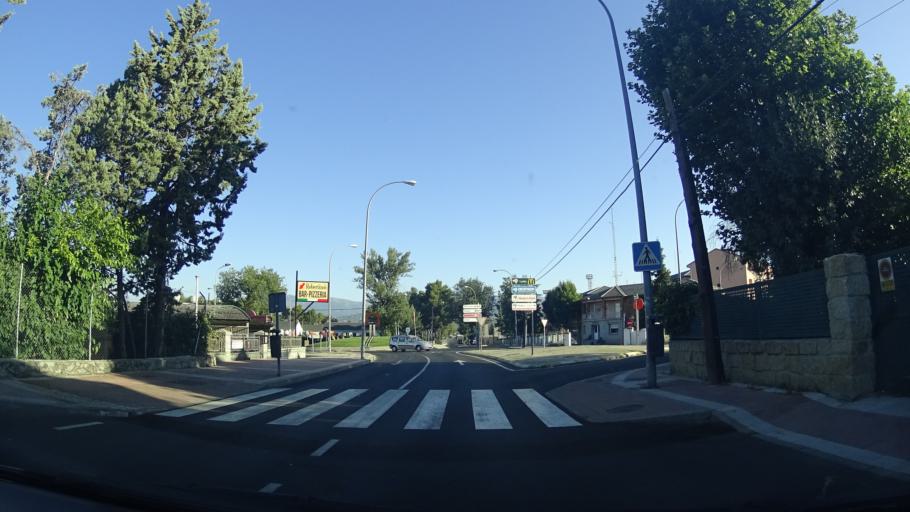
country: ES
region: Madrid
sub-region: Provincia de Madrid
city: Collado-Villalba
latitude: 40.6376
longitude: -4.0037
